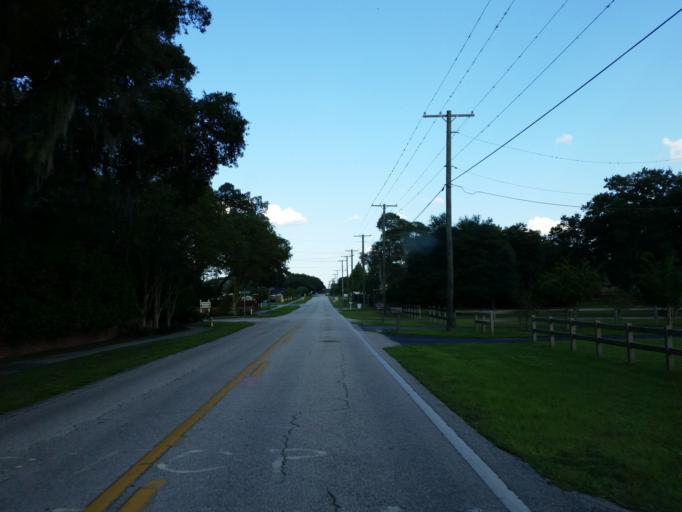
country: US
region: Florida
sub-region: Hillsborough County
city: Bloomingdale
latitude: 27.9083
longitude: -82.2664
